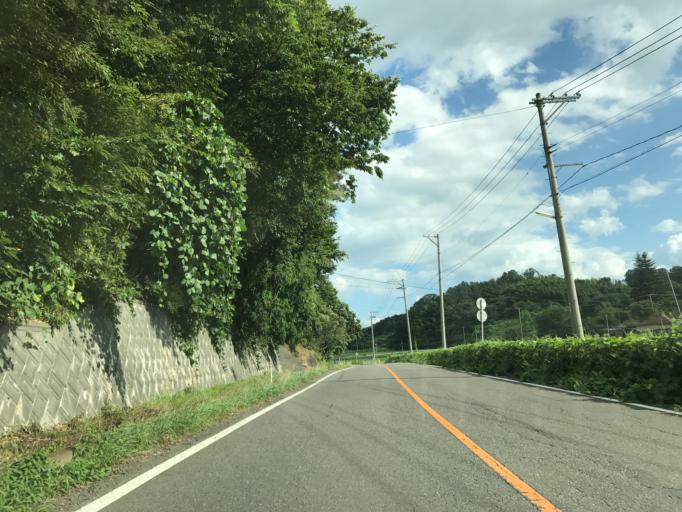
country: JP
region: Fukushima
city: Koriyama
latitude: 37.4077
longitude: 140.4345
